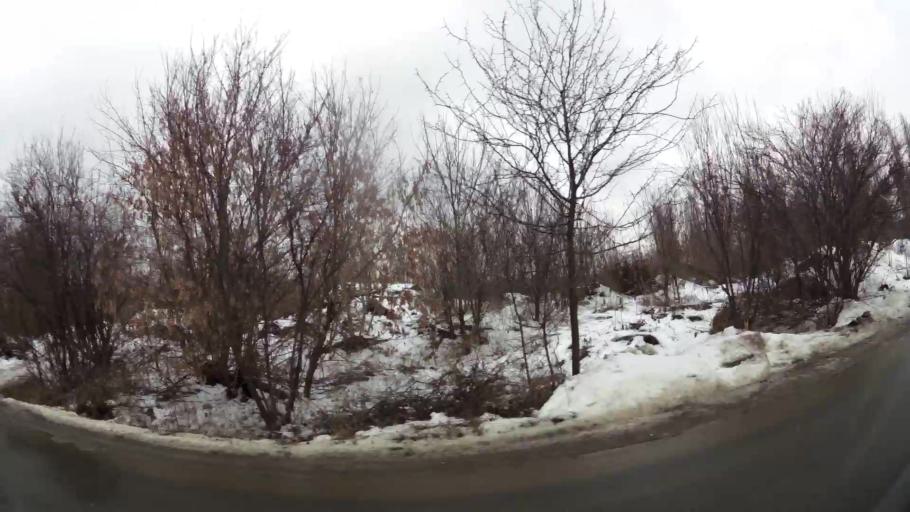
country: RO
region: Ilfov
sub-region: Comuna Chitila
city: Chitila
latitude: 44.4998
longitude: 26.0069
